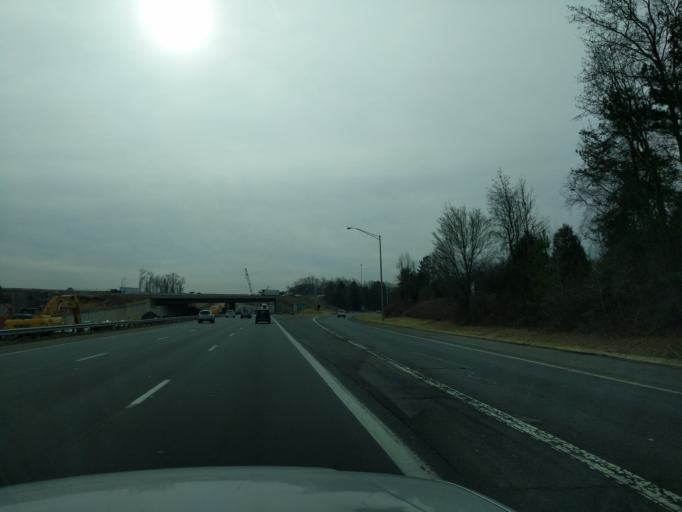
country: US
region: North Carolina
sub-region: Mecklenburg County
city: Charlotte
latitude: 35.2792
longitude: -80.8466
